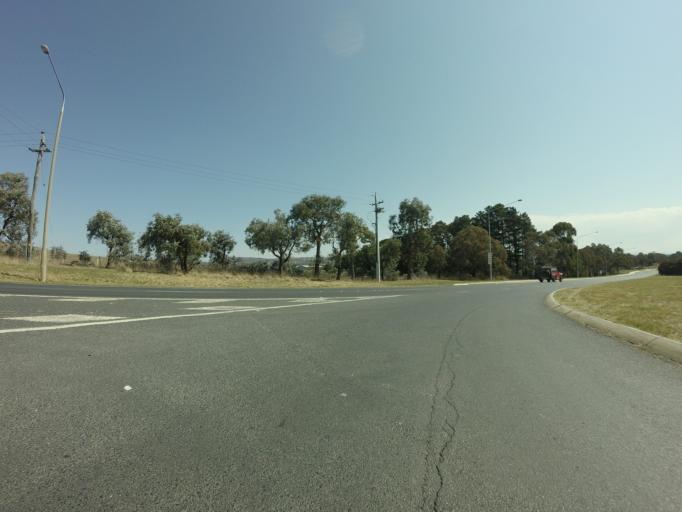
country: AU
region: Australian Capital Territory
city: Forrest
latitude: -35.3354
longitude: 149.1713
